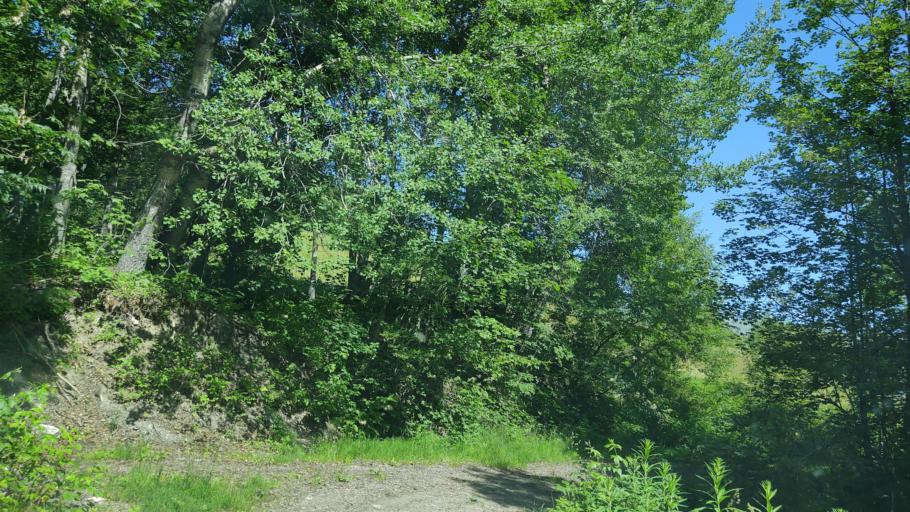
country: FR
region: Rhone-Alpes
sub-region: Departement de la Savoie
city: Saint-Jean-de-Maurienne
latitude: 45.2285
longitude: 6.2727
